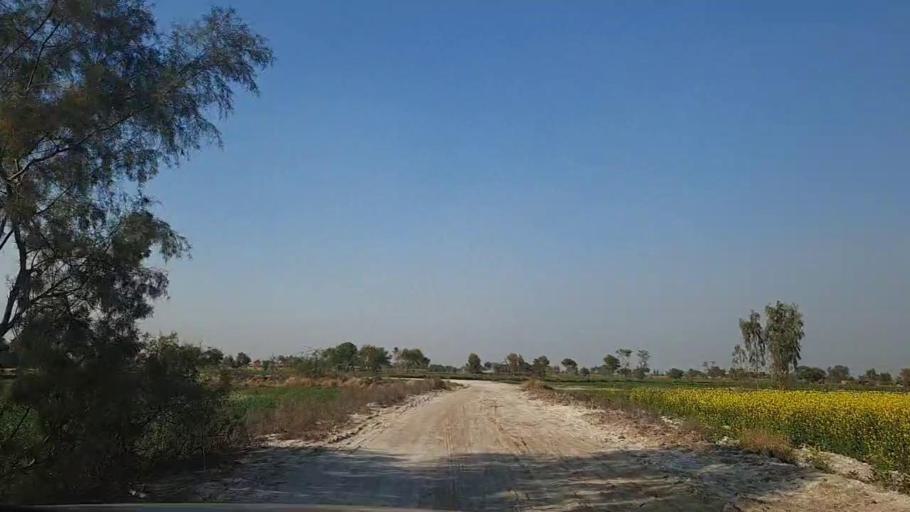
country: PK
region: Sindh
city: Daur
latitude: 26.3288
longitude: 68.1770
